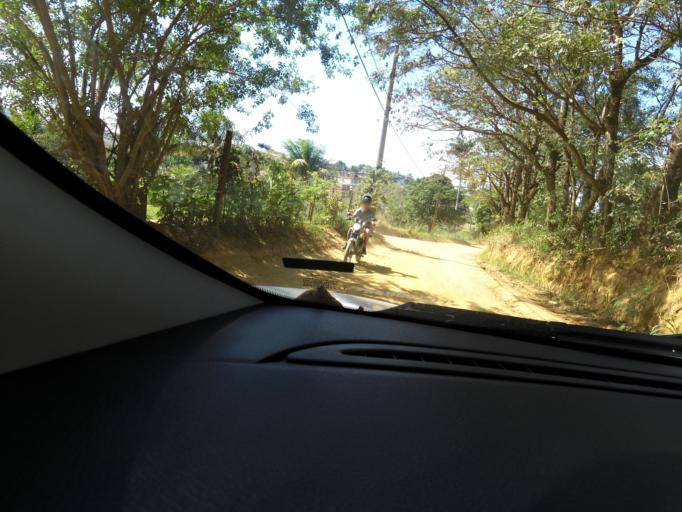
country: BR
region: Espirito Santo
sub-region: Guarapari
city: Guarapari
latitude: -20.6486
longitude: -40.5182
